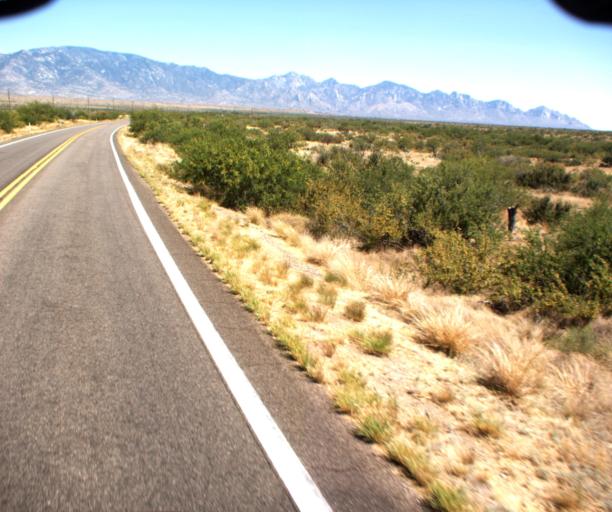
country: US
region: Arizona
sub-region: Pima County
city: Catalina
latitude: 32.5803
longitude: -110.9523
